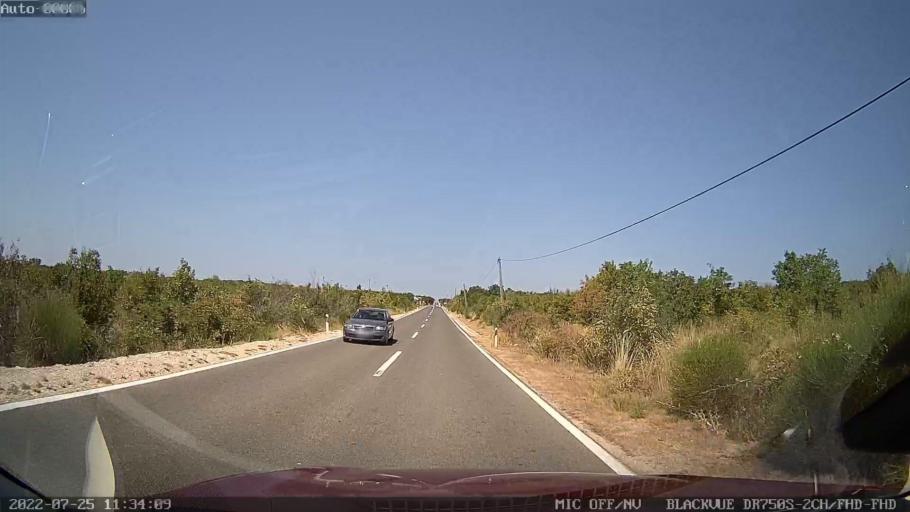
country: HR
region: Zadarska
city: Posedarje
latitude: 44.2289
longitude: 15.4252
